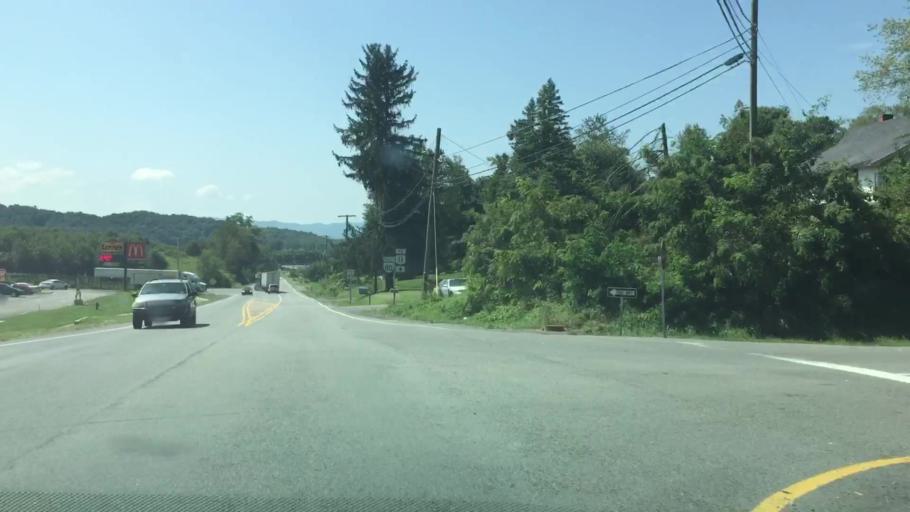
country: US
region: Virginia
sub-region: Washington County
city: Emory
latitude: 36.7569
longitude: -81.8570
